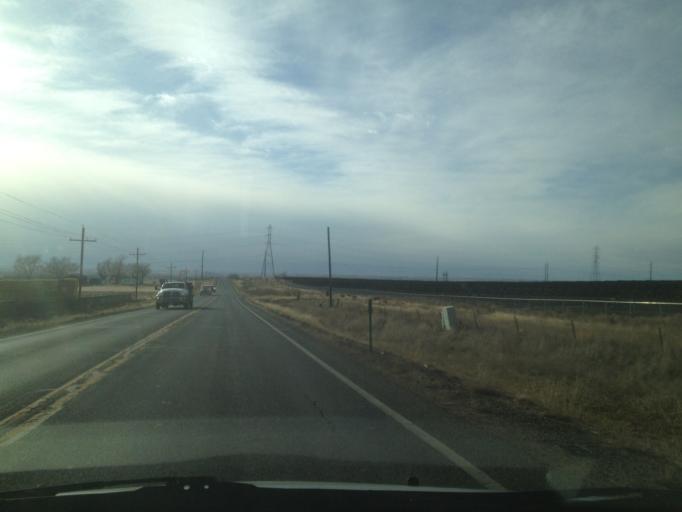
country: US
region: Colorado
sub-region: Weld County
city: Aristocrat Ranchettes
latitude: 40.0804
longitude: -104.7475
